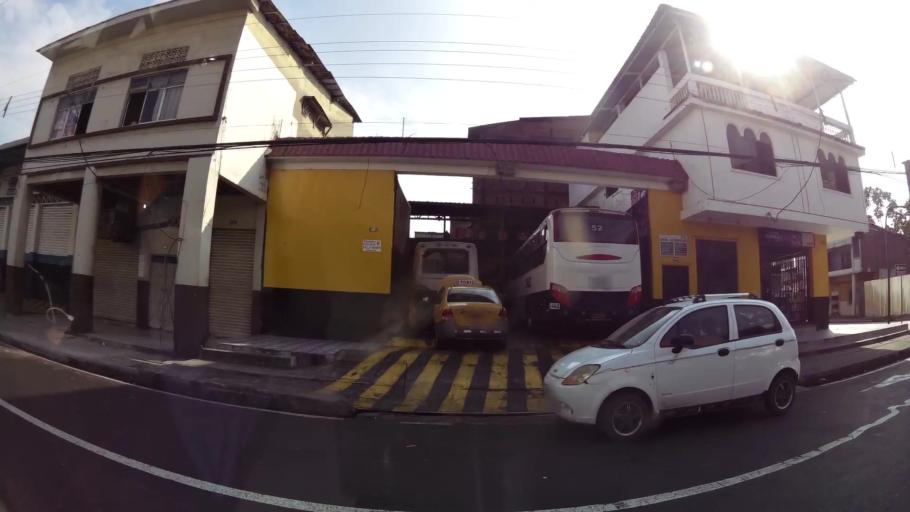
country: EC
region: Guayas
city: Guayaquil
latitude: -2.1942
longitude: -79.8947
